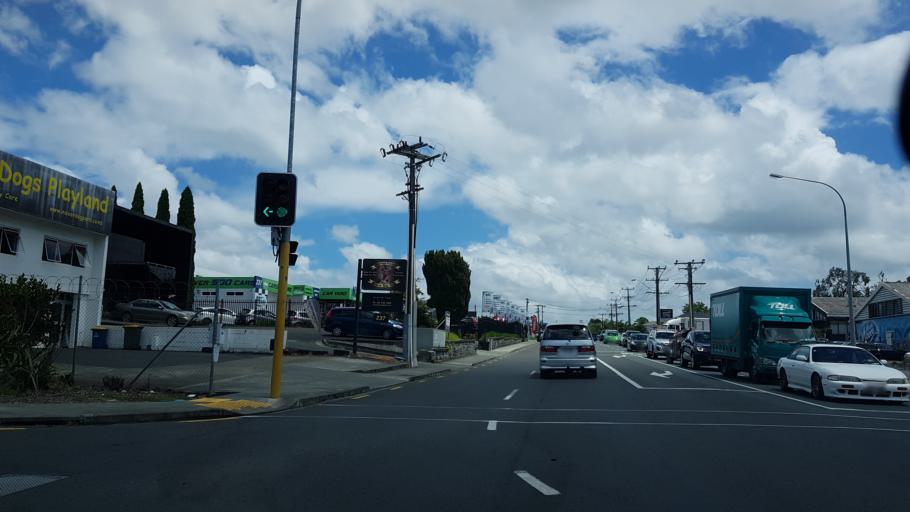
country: NZ
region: Auckland
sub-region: Auckland
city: North Shore
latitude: -36.7783
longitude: 174.7426
